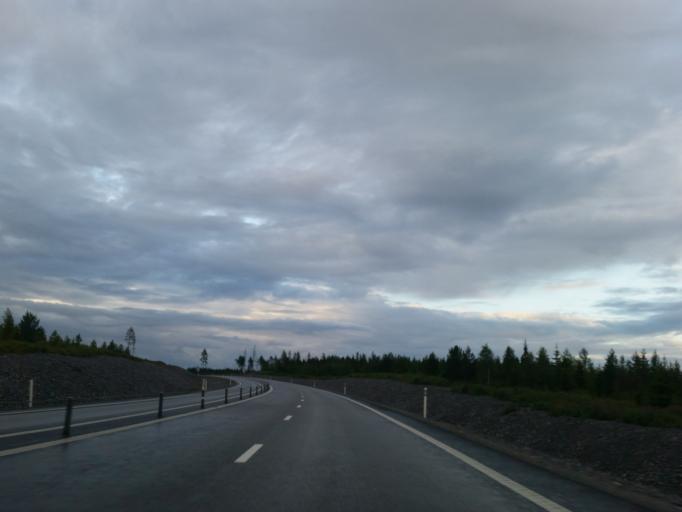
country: SE
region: Vaesterbotten
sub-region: Umea Kommun
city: Umea
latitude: 63.8552
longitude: 20.2627
